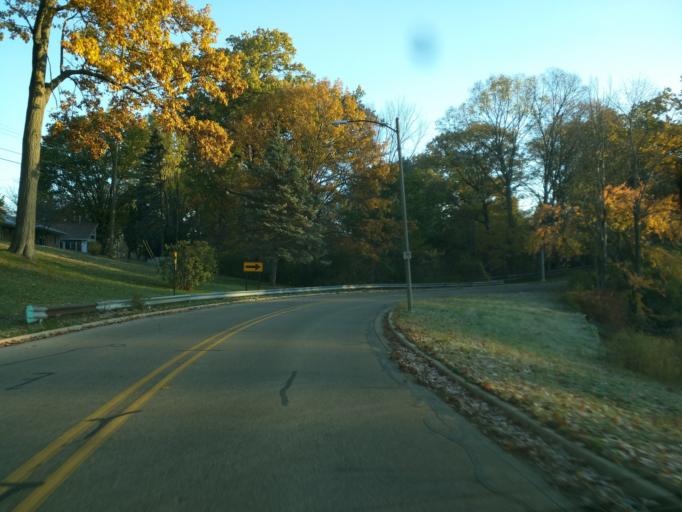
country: US
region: Michigan
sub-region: Ingham County
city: Edgemont Park
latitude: 42.7600
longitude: -84.5788
